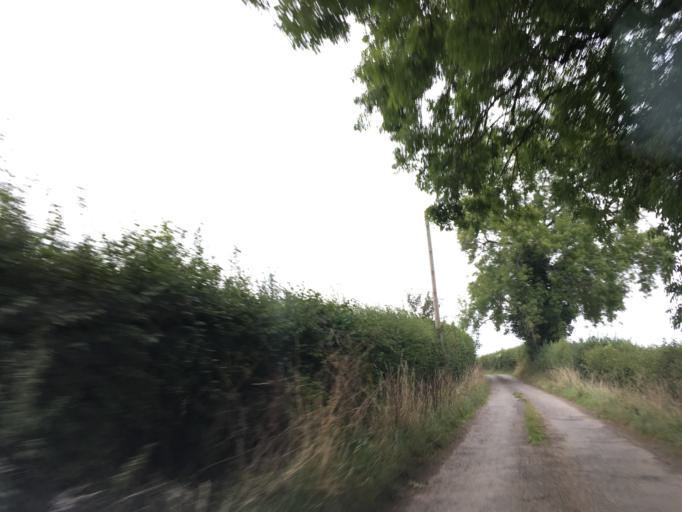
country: GB
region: England
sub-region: South Gloucestershire
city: Falfield
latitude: 51.6432
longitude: -2.4632
